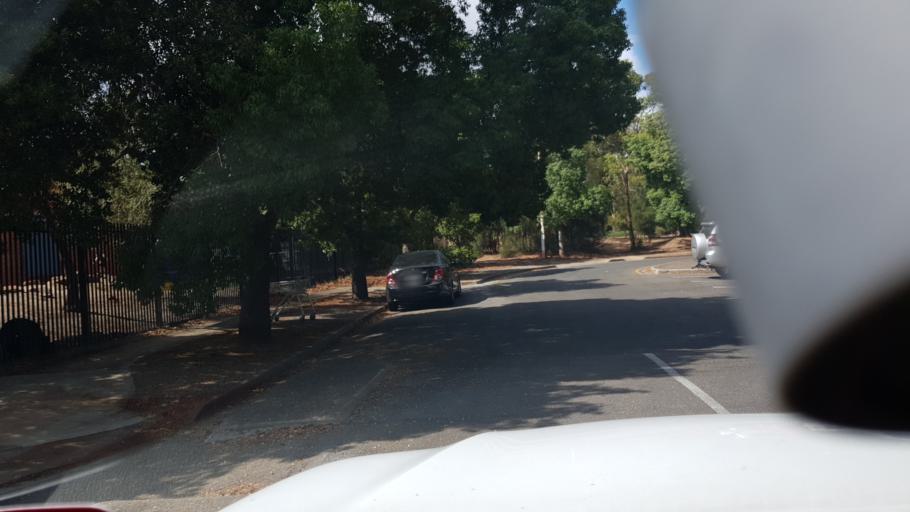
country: AU
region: South Australia
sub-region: Holdfast Bay
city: Seacliff Park
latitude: -35.0248
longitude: 138.5293
